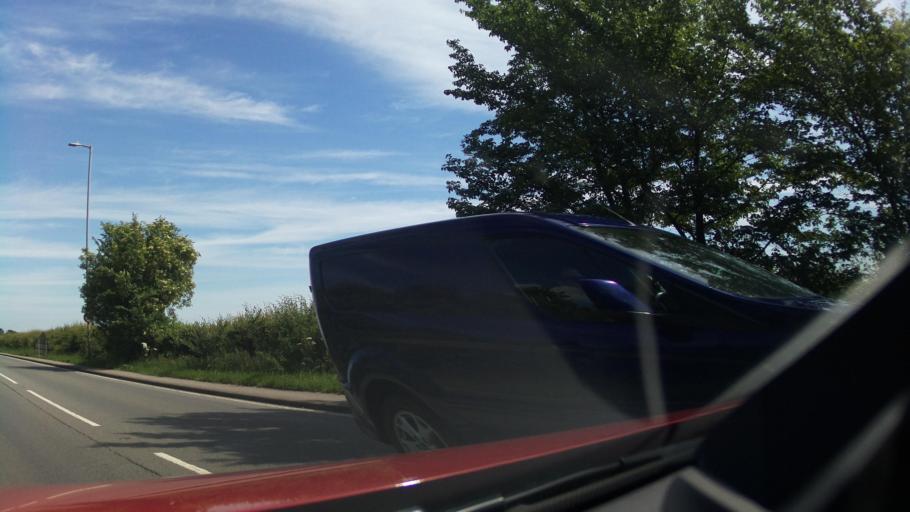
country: GB
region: England
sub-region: Lincolnshire
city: Burton
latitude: 53.2961
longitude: -0.5411
